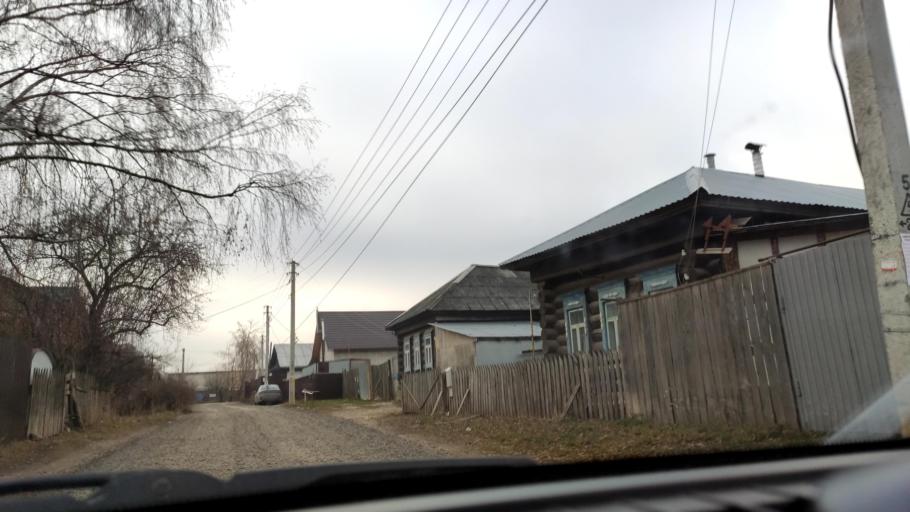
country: RU
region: Perm
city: Kondratovo
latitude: 57.9573
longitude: 56.1733
